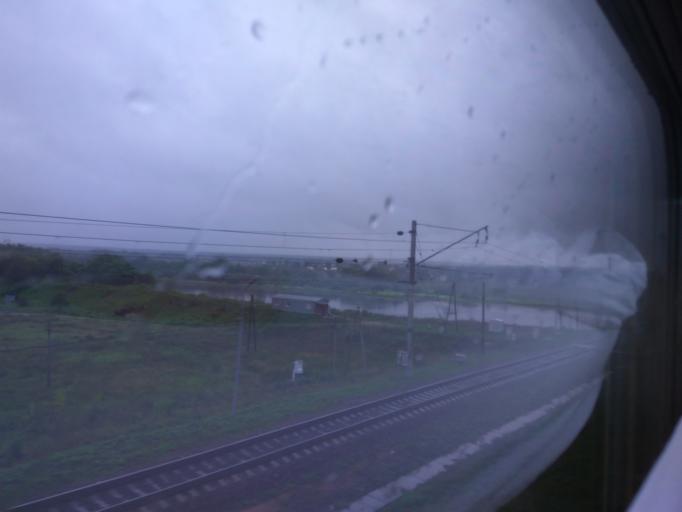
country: RU
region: Moskovskaya
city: Kashira
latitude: 54.8590
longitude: 38.1694
